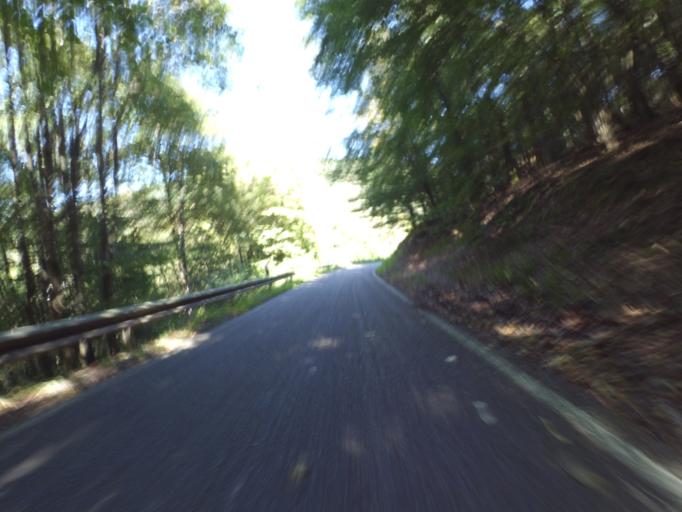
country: DE
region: Rheinland-Pfalz
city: Bad Bertrich
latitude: 50.0695
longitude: 7.0242
